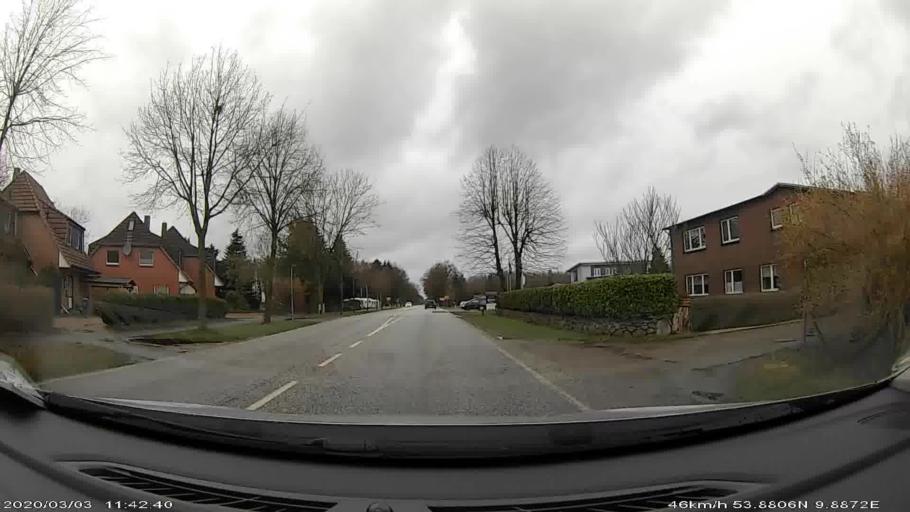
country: DE
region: Schleswig-Holstein
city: Lentfohrden
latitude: 53.8821
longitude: 9.8870
